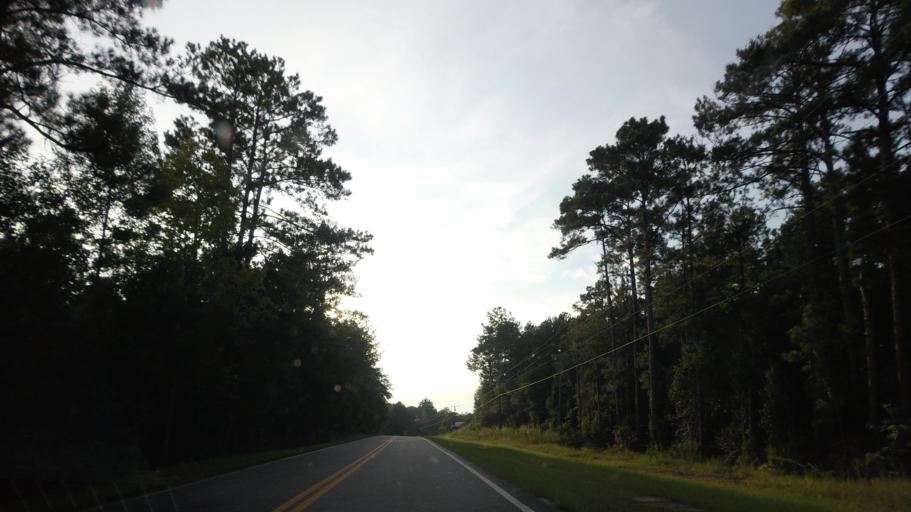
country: US
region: Georgia
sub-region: Wilkinson County
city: Gordon
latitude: 32.8236
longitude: -83.4086
